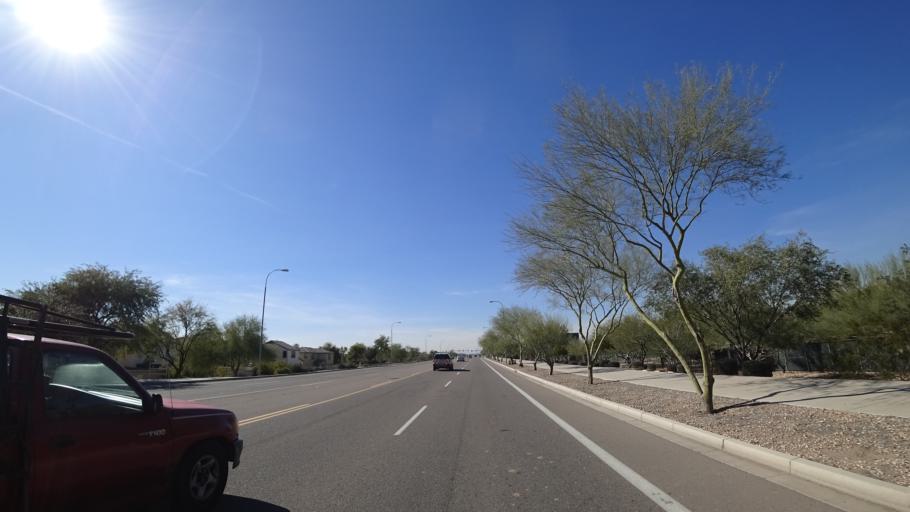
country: US
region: Arizona
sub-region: Maricopa County
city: Litchfield Park
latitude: 33.5081
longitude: -112.2946
